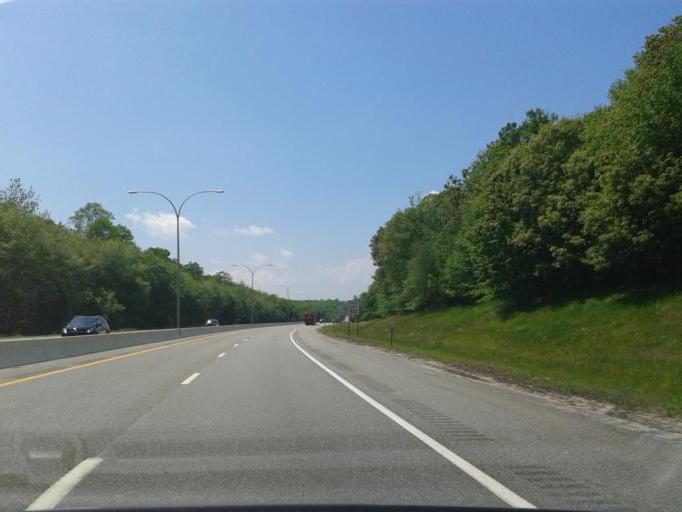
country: US
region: Rhode Island
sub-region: Washington County
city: North Kingstown
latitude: 41.5269
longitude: -71.4343
